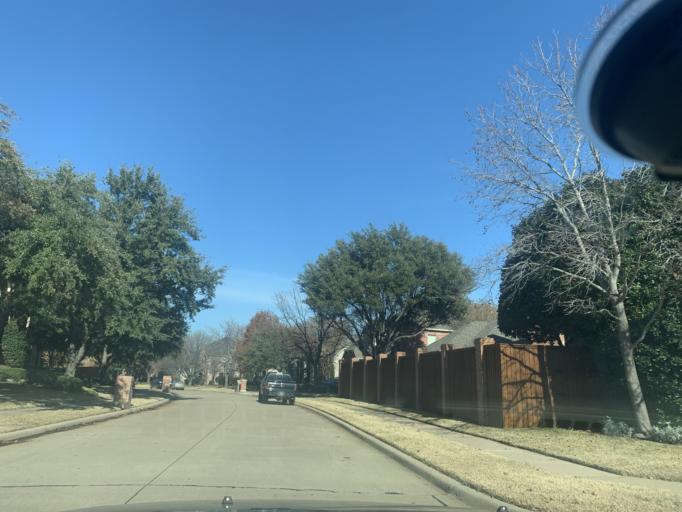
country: US
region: Texas
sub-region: Denton County
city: The Colony
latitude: 33.0529
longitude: -96.8143
